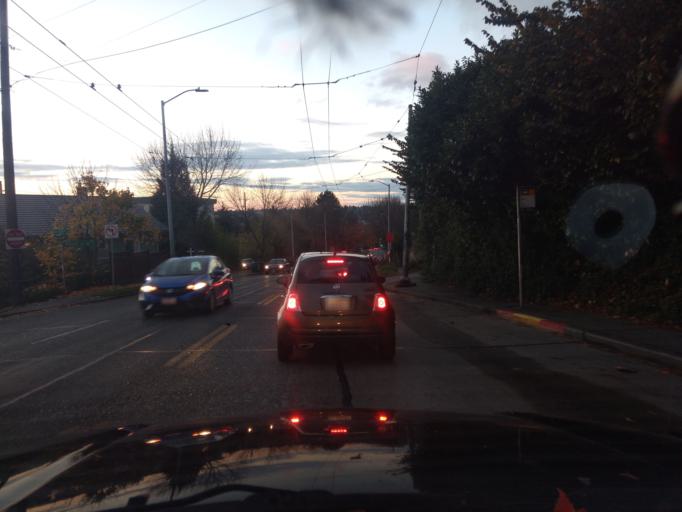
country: US
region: Washington
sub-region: King County
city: Seattle
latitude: 47.6650
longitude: -122.3595
